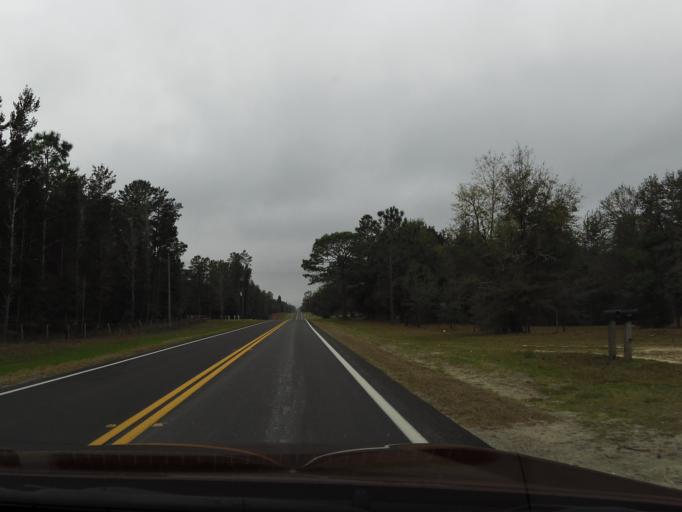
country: US
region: Florida
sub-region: Gilchrist County
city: Trenton
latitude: 29.7962
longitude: -82.8463
